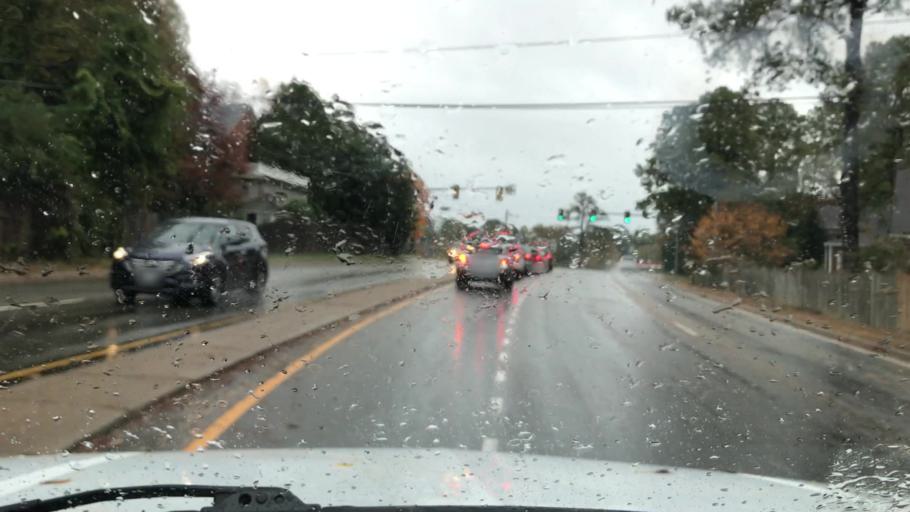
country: US
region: Virginia
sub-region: Henrico County
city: Tuckahoe
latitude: 37.5929
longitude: -77.5355
